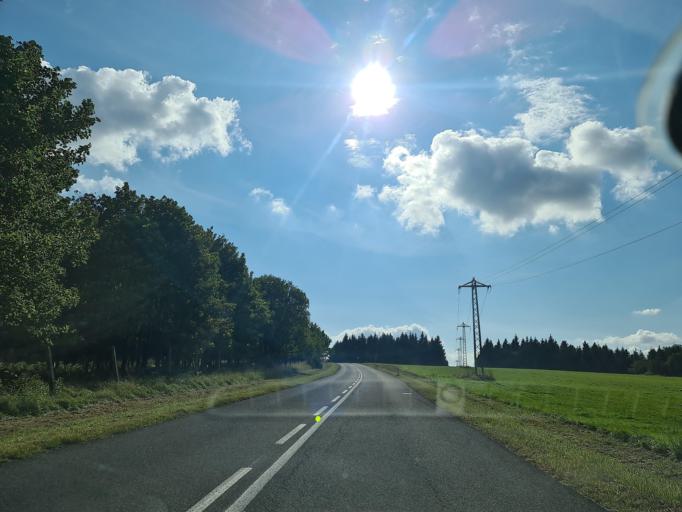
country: CZ
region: Ustecky
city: Mezibori
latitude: 50.6380
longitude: 13.5458
